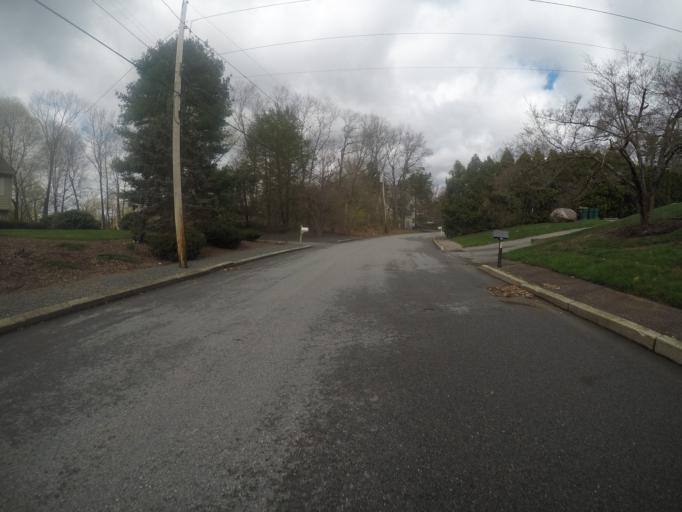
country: US
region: Massachusetts
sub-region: Bristol County
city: Easton
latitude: 42.0311
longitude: -71.1300
